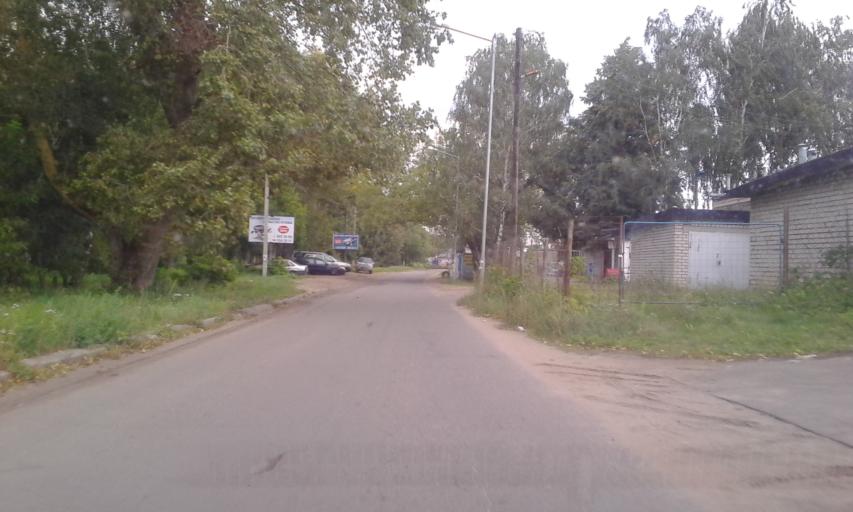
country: BY
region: Minsk
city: Minsk
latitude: 53.9436
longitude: 27.5682
